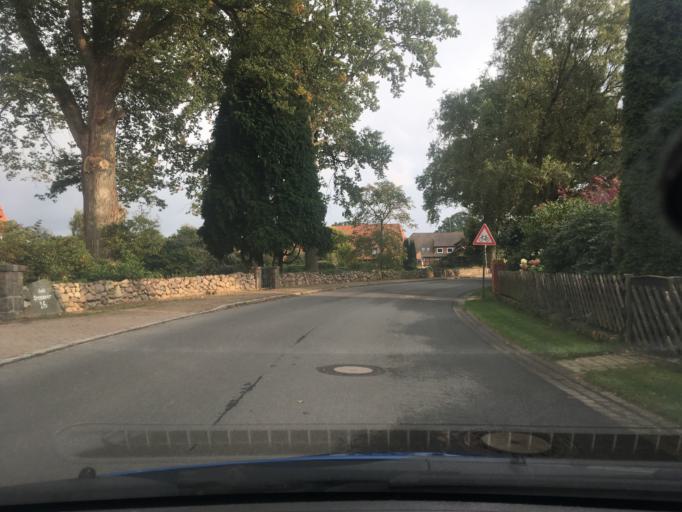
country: DE
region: Lower Saxony
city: Eyendorf
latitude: 53.1759
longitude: 10.1586
